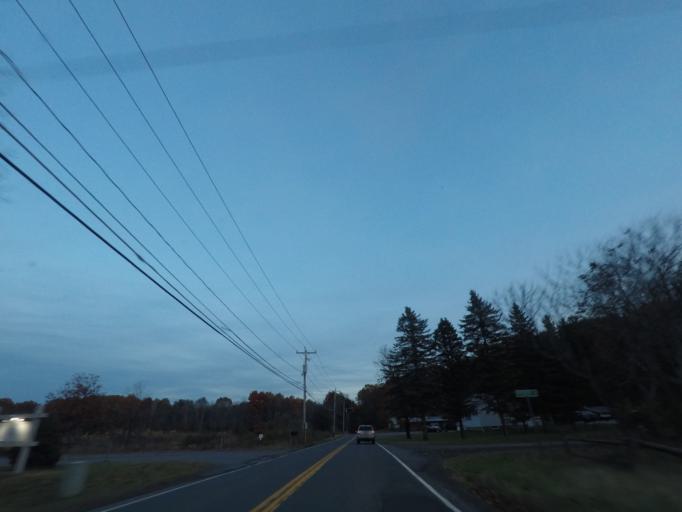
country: US
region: New York
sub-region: Albany County
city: Westmere
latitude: 42.7463
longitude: -73.9078
